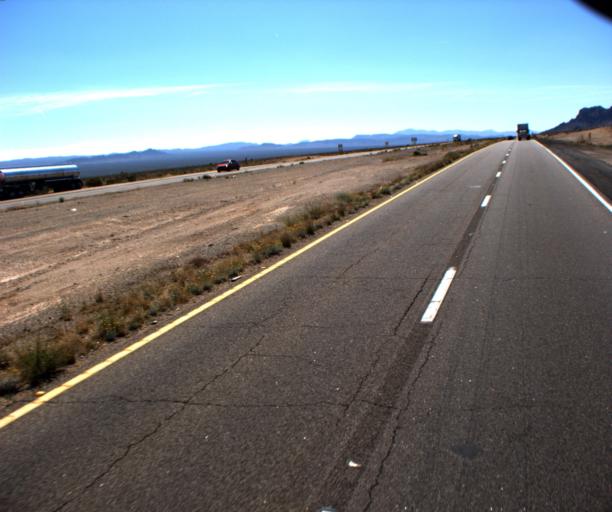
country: US
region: Nevada
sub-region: Clark County
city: Boulder City
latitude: 35.8362
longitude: -114.5672
